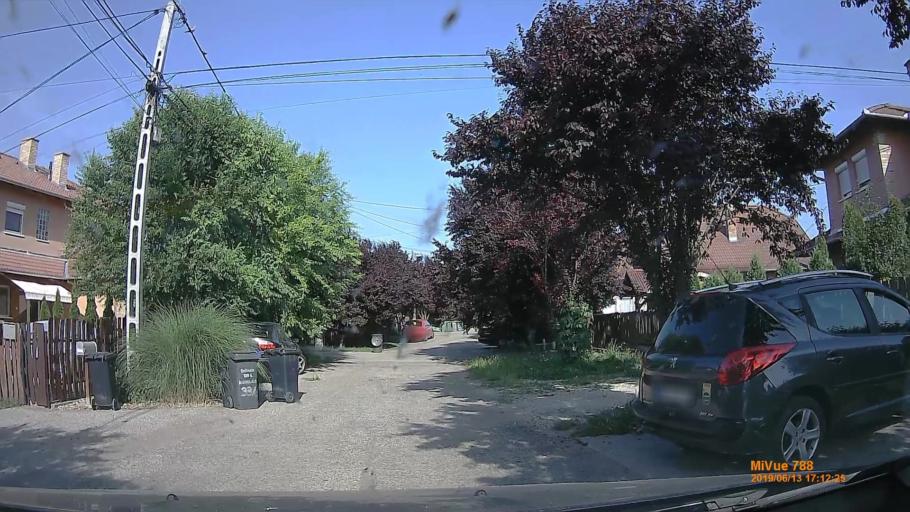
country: HU
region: Pest
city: Gyomro
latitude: 47.4154
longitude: 19.3987
